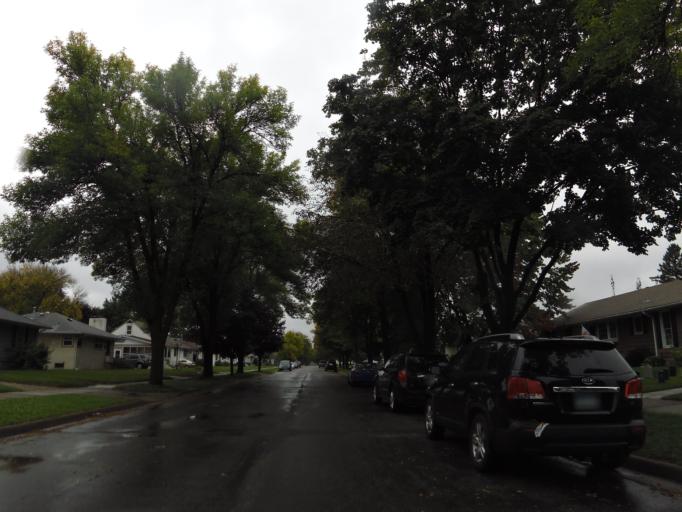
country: US
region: Minnesota
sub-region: Dakota County
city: Inver Grove Heights
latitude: 44.8691
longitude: -93.0375
